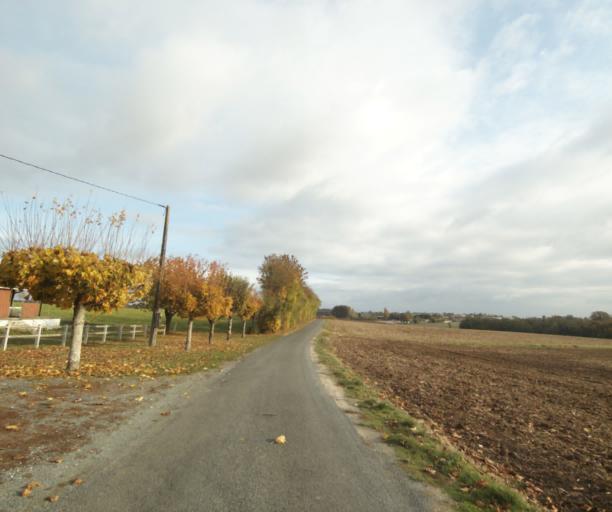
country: FR
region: Poitou-Charentes
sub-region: Departement de la Charente-Maritime
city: Saint-Georges-des-Coteaux
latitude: 45.7821
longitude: -0.7285
